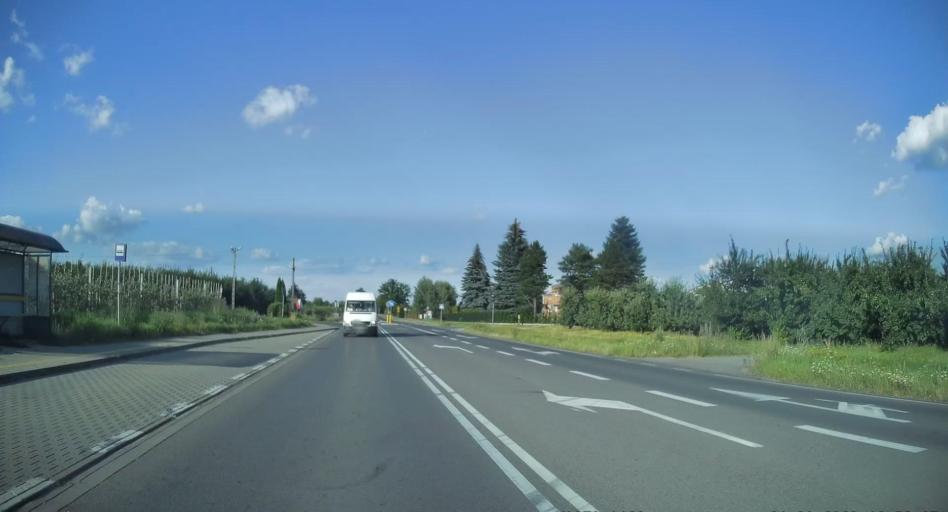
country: PL
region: Masovian Voivodeship
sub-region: Powiat grojecki
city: Belsk Duzy
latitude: 51.8448
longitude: 20.8337
